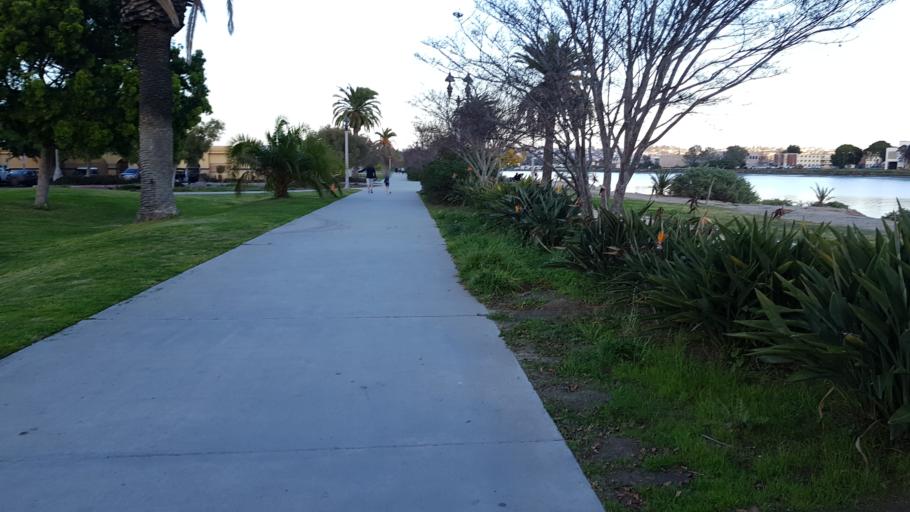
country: US
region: California
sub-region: San Diego County
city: Coronado
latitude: 32.7324
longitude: -117.2144
